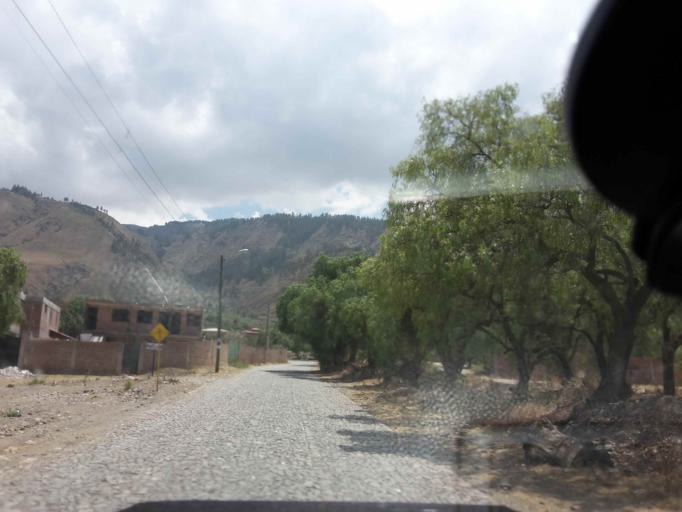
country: BO
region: Cochabamba
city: Cochabamba
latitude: -17.3262
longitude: -66.2231
